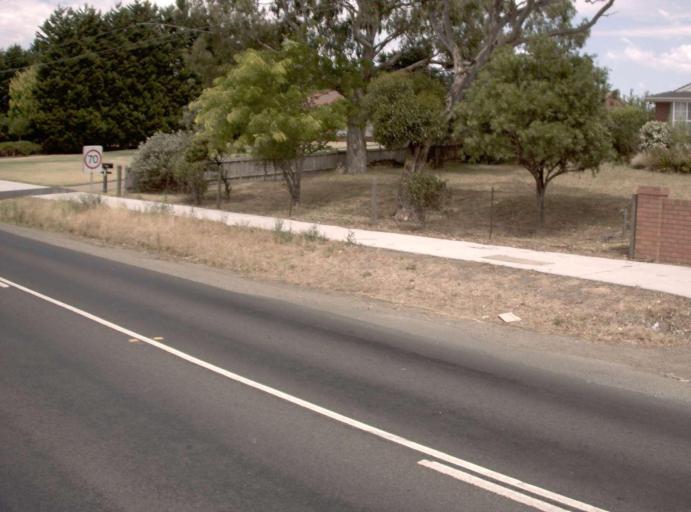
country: AU
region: Victoria
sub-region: Casey
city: Hallam
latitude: -38.0294
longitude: 145.2761
